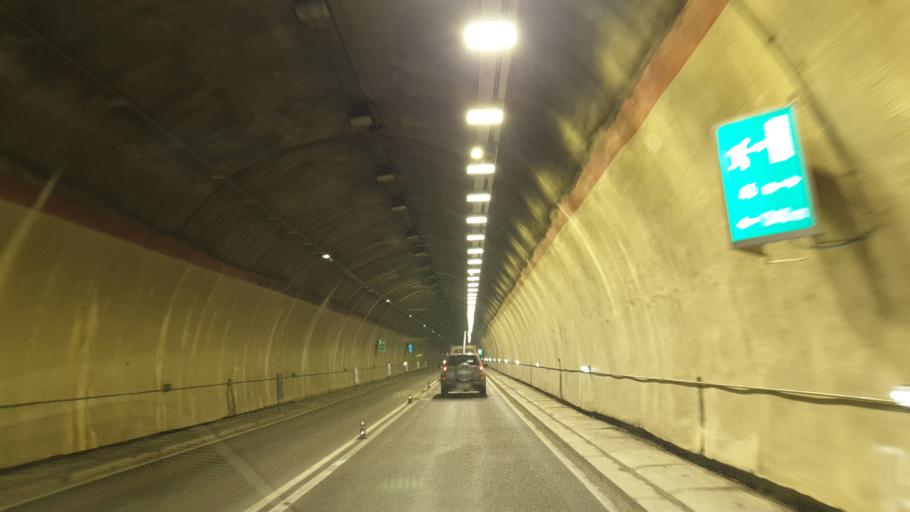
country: IT
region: Veneto
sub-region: Provincia di Belluno
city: Perarolo di Cadore
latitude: 46.3821
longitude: 12.3583
